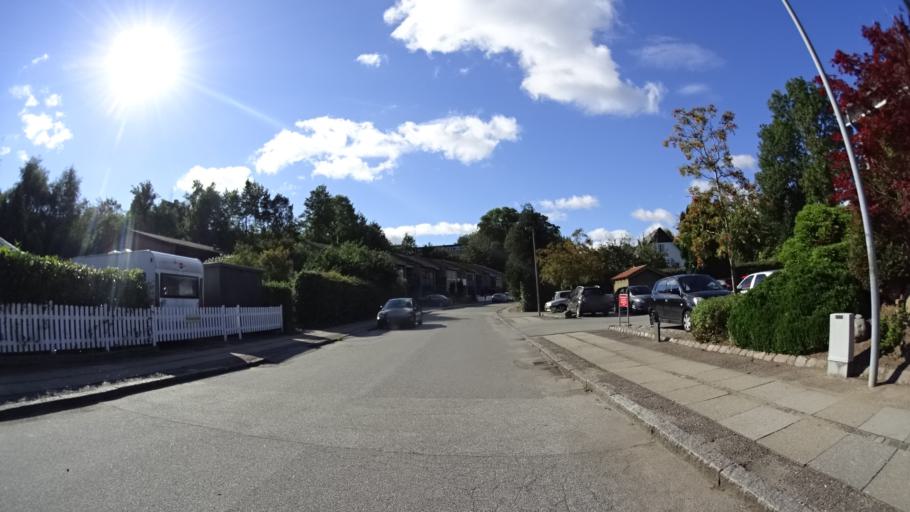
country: DK
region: Central Jutland
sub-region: Arhus Kommune
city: Stavtrup
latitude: 56.1224
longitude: 10.1528
